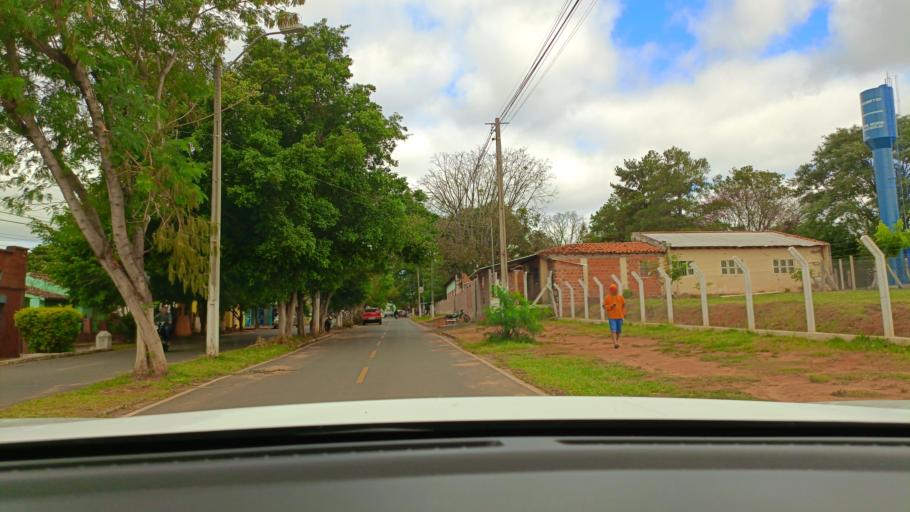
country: PY
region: San Pedro
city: Guayaybi
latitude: -24.6602
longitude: -56.4429
